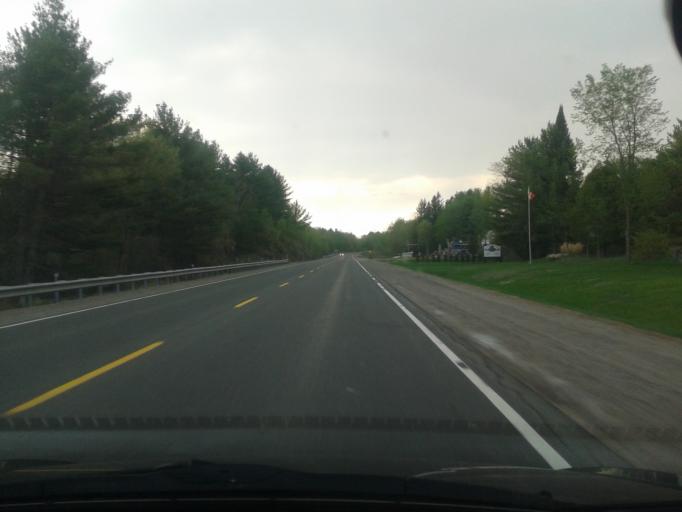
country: CA
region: Ontario
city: Belleville
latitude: 44.5410
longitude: -77.3568
